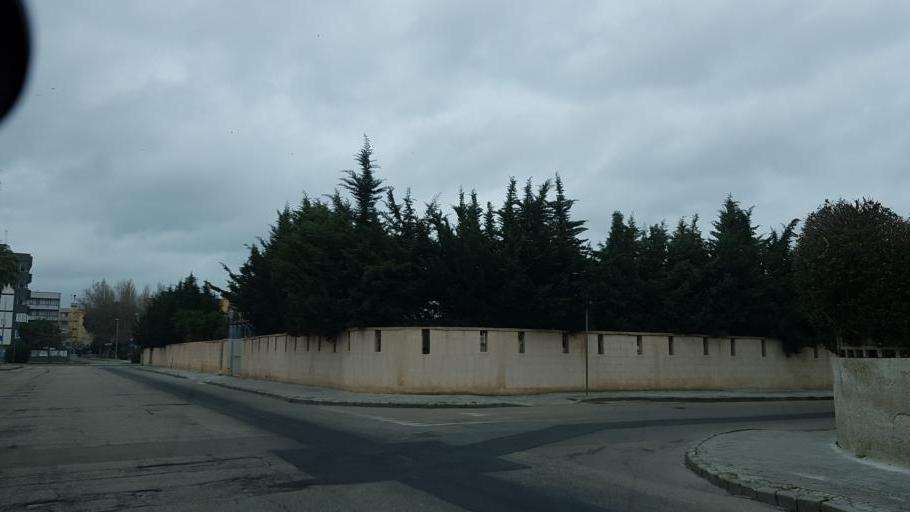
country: IT
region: Apulia
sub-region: Provincia di Brindisi
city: Brindisi
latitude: 40.6170
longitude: 17.9267
